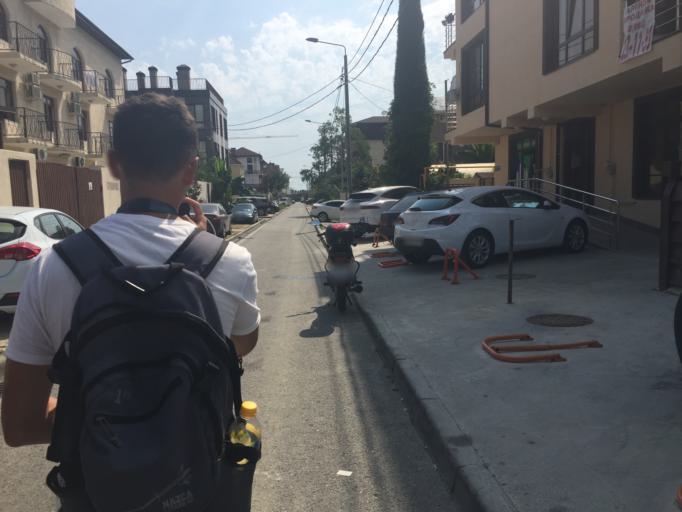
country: RU
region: Krasnodarskiy
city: Adler
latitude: 43.4145
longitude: 39.9622
